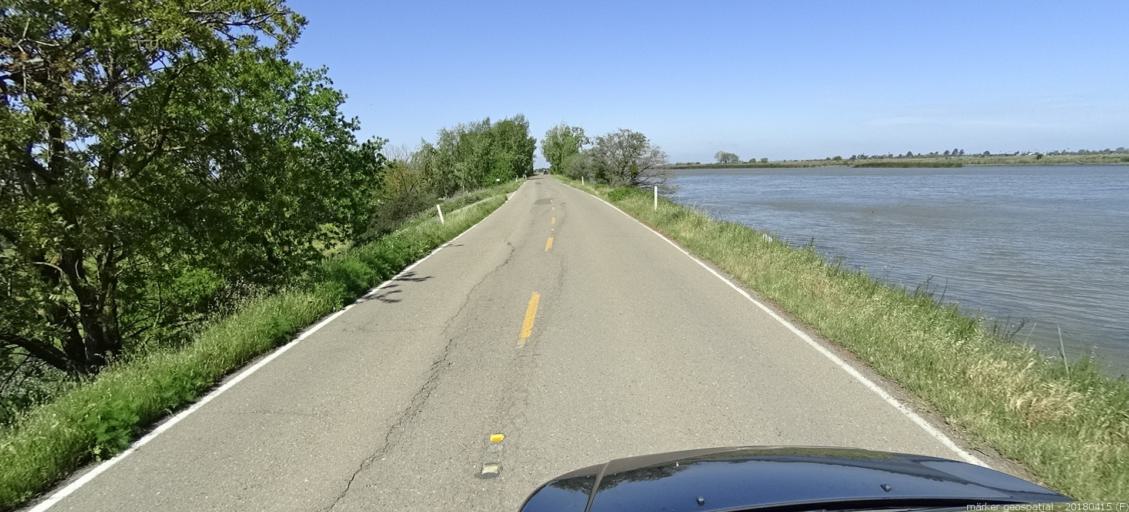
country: US
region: California
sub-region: Contra Costa County
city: Bethel Island
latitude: 38.1069
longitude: -121.5734
